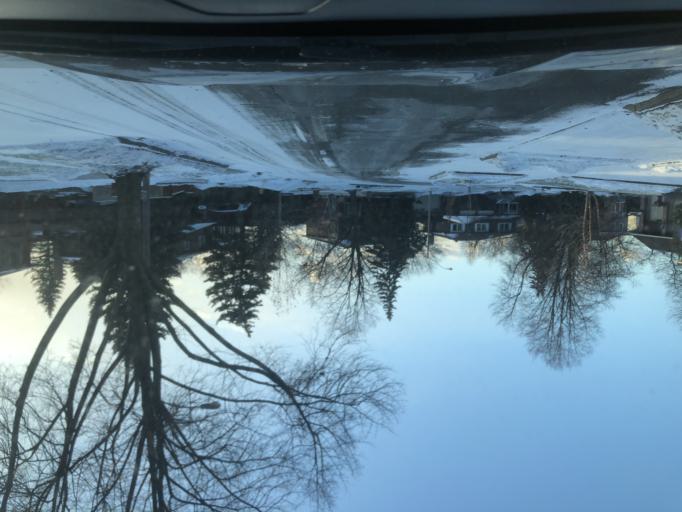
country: CA
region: Ontario
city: Scarborough
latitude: 43.7840
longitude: -79.1546
